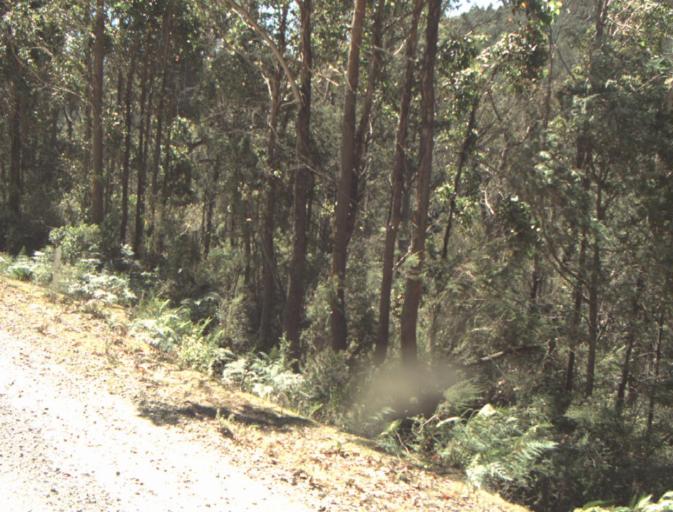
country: AU
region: Tasmania
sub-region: Dorset
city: Scottsdale
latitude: -41.3901
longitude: 147.5091
